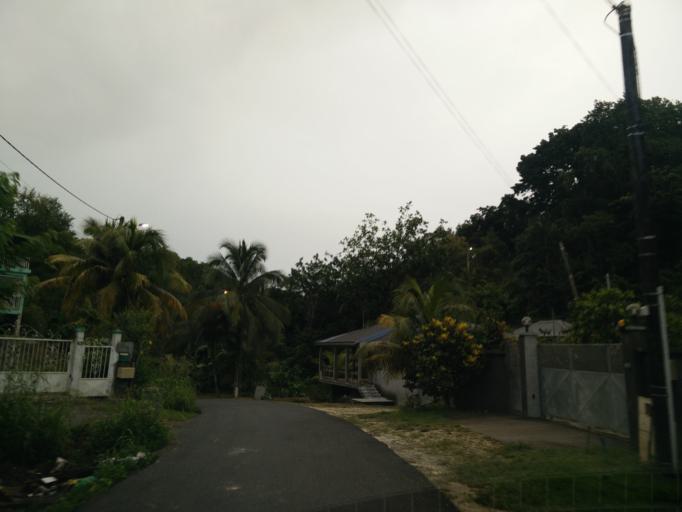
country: GP
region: Guadeloupe
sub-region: Guadeloupe
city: Le Gosier
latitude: 16.2350
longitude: -61.4920
